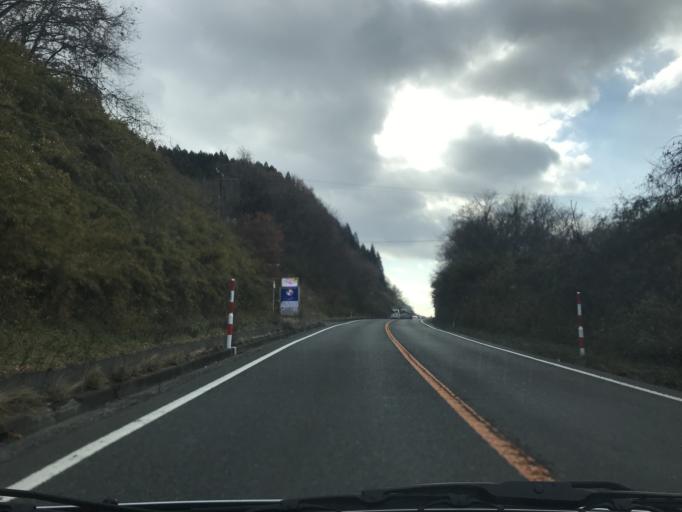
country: JP
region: Iwate
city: Ichinoseki
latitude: 38.8971
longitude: 141.1148
